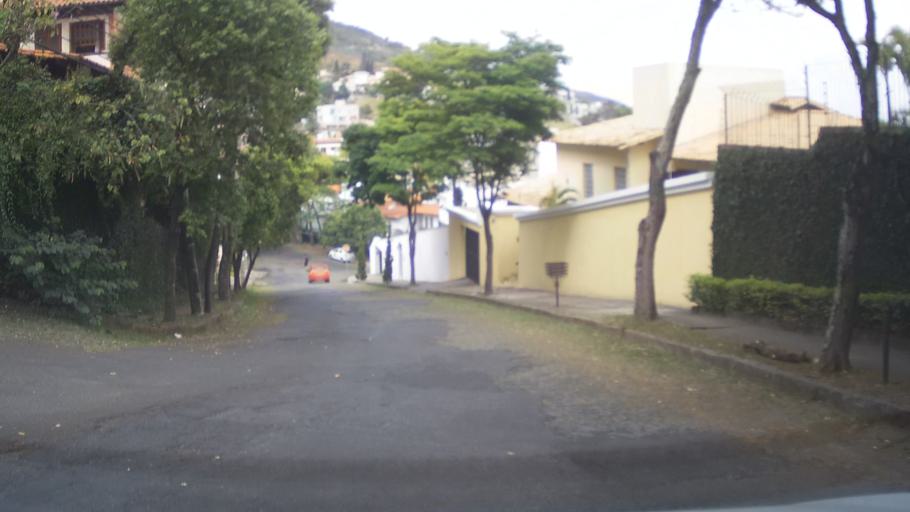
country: BR
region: Minas Gerais
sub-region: Belo Horizonte
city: Belo Horizonte
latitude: -19.9522
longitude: -43.9197
